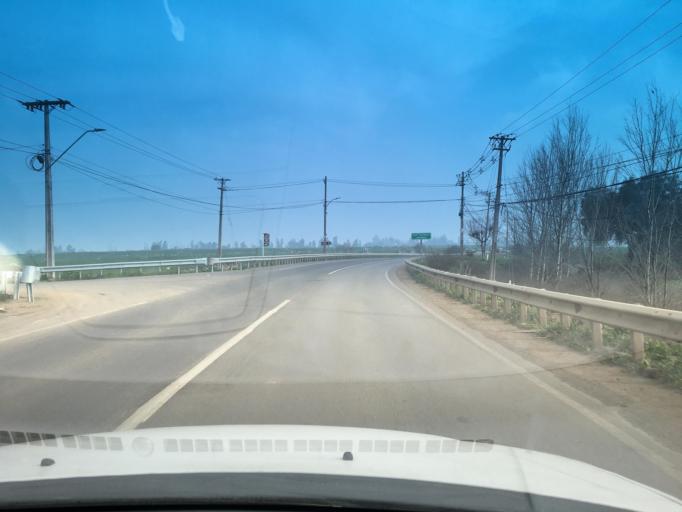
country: CL
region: Santiago Metropolitan
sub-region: Provincia de Chacabuco
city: Lampa
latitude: -33.3504
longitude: -70.8039
